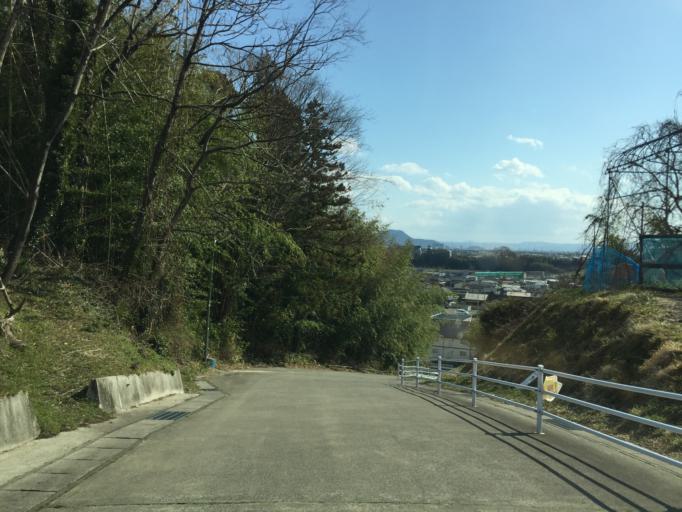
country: JP
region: Fukushima
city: Fukushima-shi
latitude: 37.8305
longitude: 140.4442
